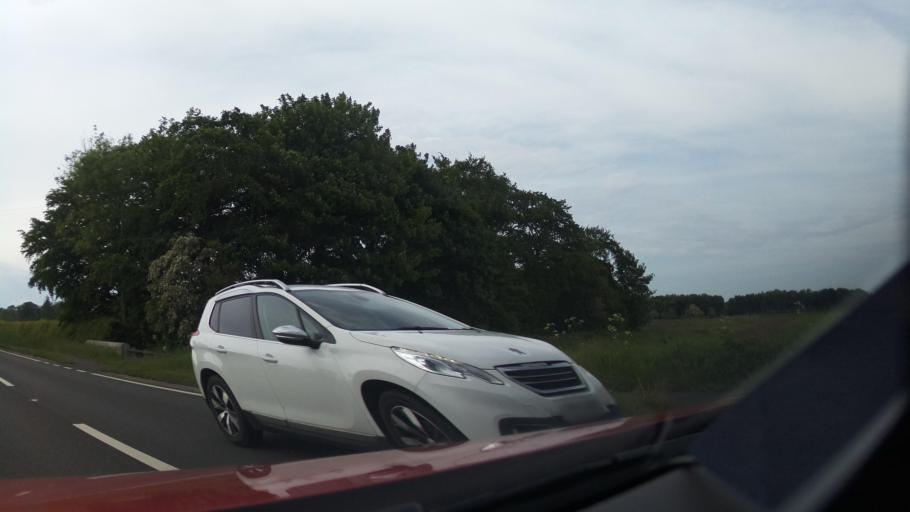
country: GB
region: England
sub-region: Northumberland
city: Lowick
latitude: 55.6767
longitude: -1.9253
